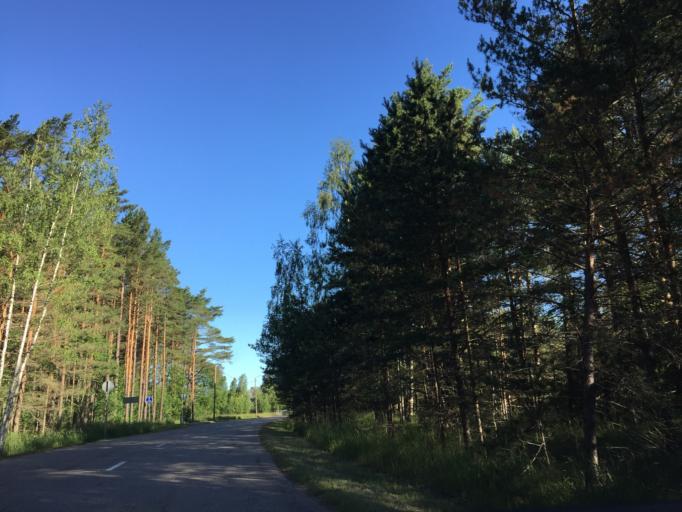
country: LV
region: Ventspils
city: Ventspils
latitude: 57.4344
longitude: 21.6257
